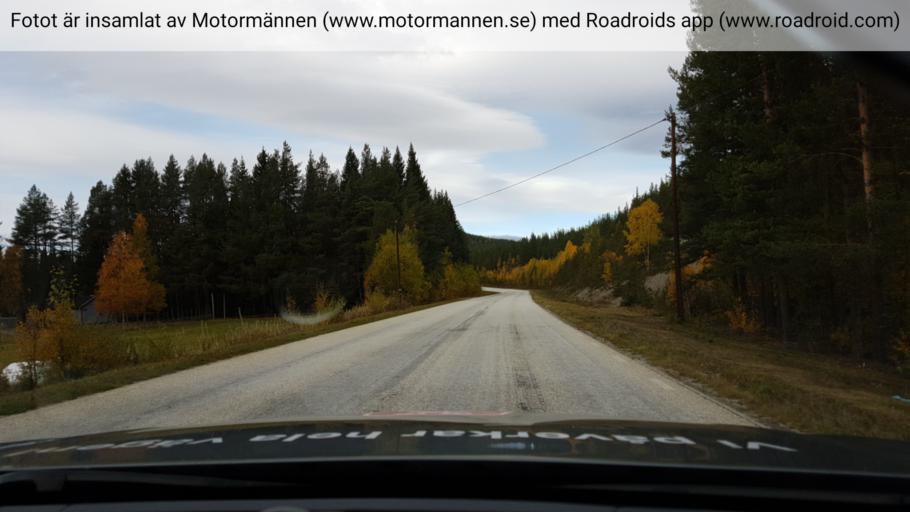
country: SE
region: Jaemtland
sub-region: Harjedalens Kommun
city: Sveg
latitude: 62.4132
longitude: 13.6360
